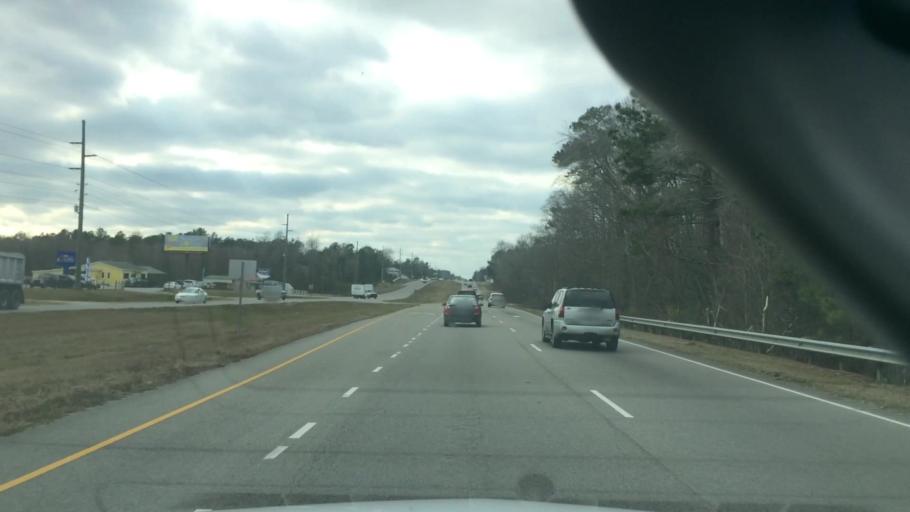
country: US
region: North Carolina
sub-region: Brunswick County
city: Shallotte
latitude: 34.0132
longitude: -78.2850
